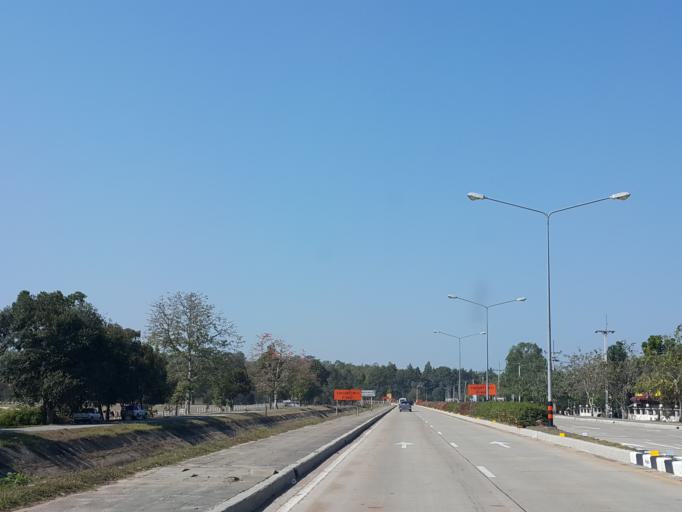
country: TH
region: Chiang Mai
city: Chiang Mai
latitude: 18.8605
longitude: 98.9608
